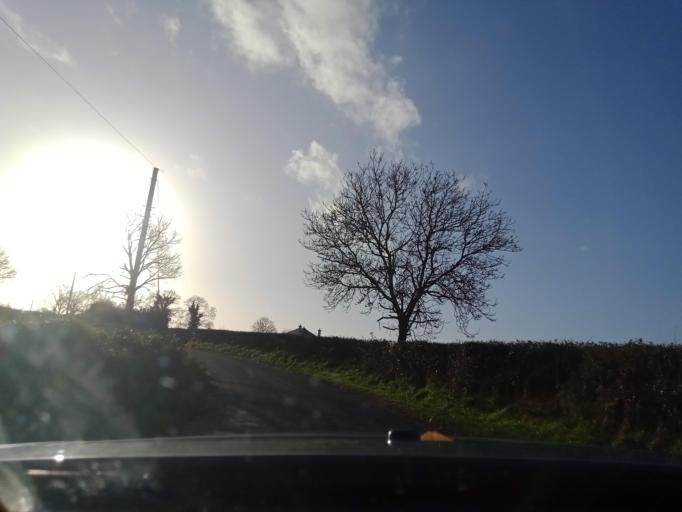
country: IE
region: Leinster
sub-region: Kilkenny
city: Callan
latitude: 52.4955
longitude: -7.3932
